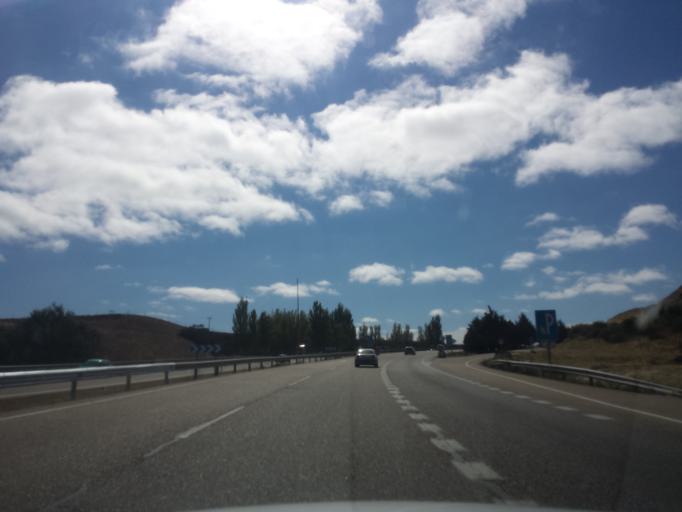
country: ES
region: Castille and Leon
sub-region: Provincia de Valladolid
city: Villardefrades
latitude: 41.7048
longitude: -5.2308
